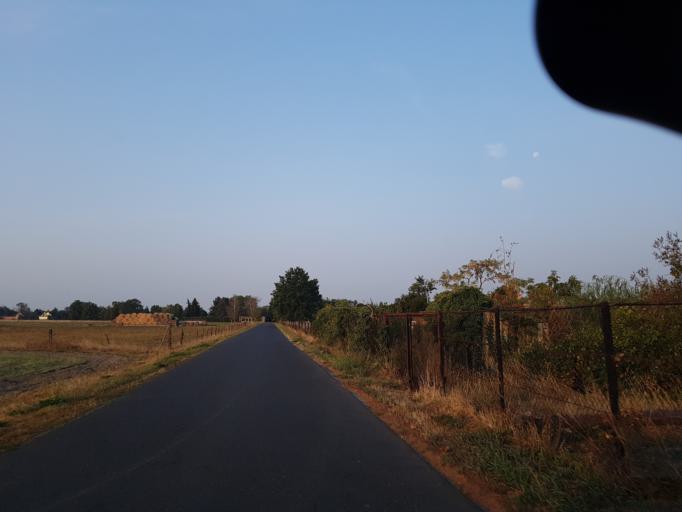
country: DE
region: Brandenburg
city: Falkenberg
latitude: 51.5421
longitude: 13.2861
